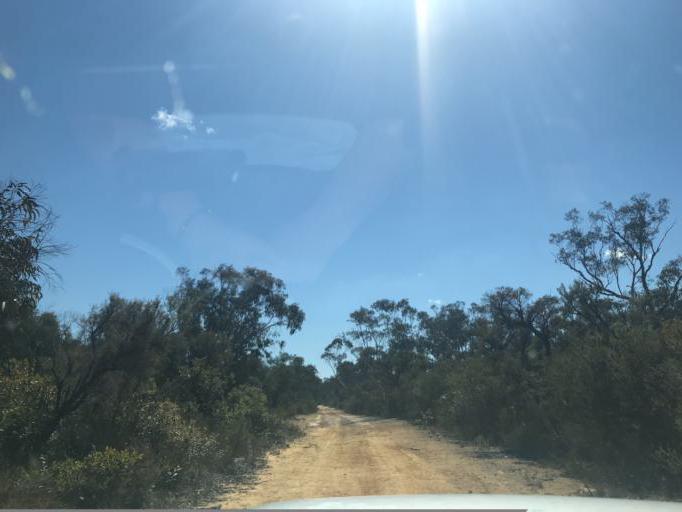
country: AU
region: New South Wales
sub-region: Wyong Shire
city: Little Jilliby
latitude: -33.1580
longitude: 151.0990
